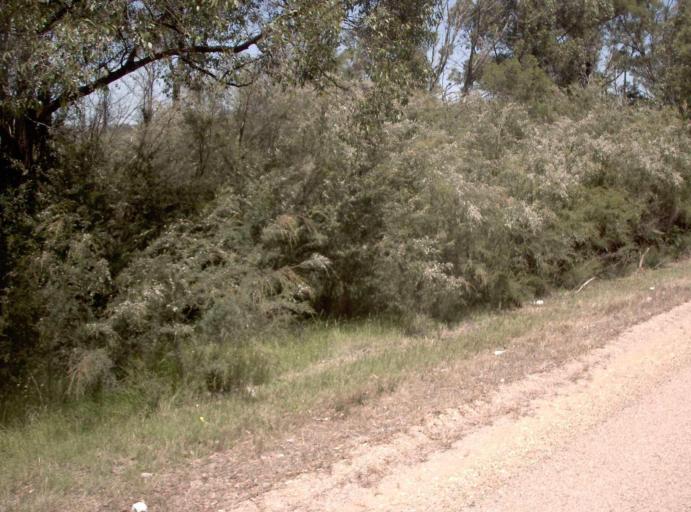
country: AU
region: Victoria
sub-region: East Gippsland
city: Bairnsdale
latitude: -37.7301
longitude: 147.7880
